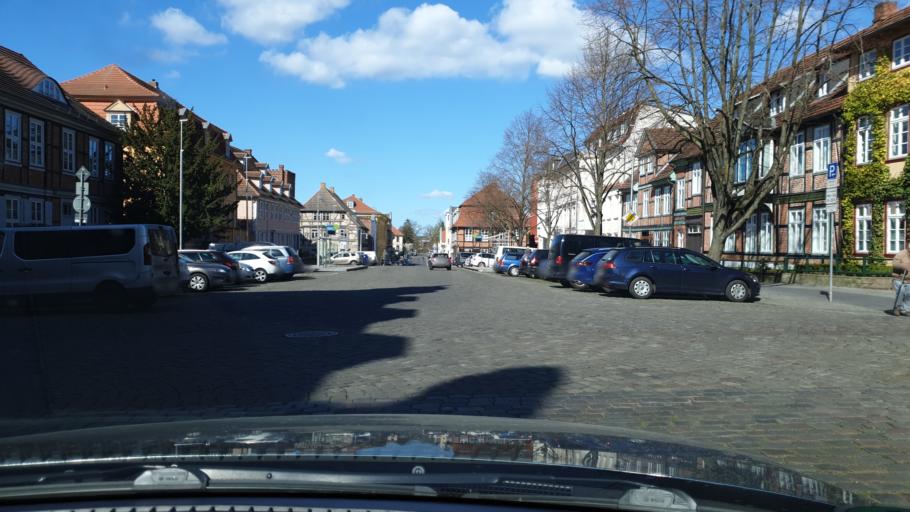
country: DE
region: Mecklenburg-Vorpommern
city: Schelfstadt
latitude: 53.6326
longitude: 11.4174
